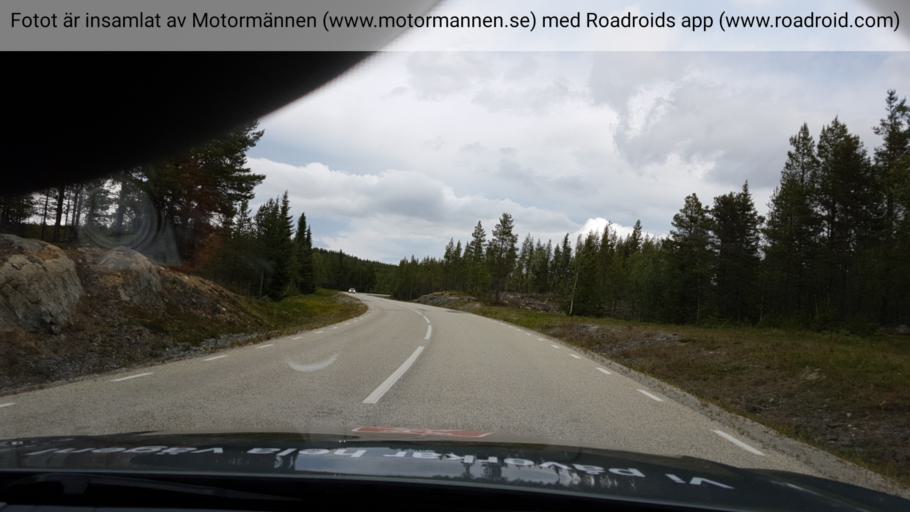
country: SE
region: Jaemtland
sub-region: Are Kommun
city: Jarpen
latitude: 62.8310
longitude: 13.2241
